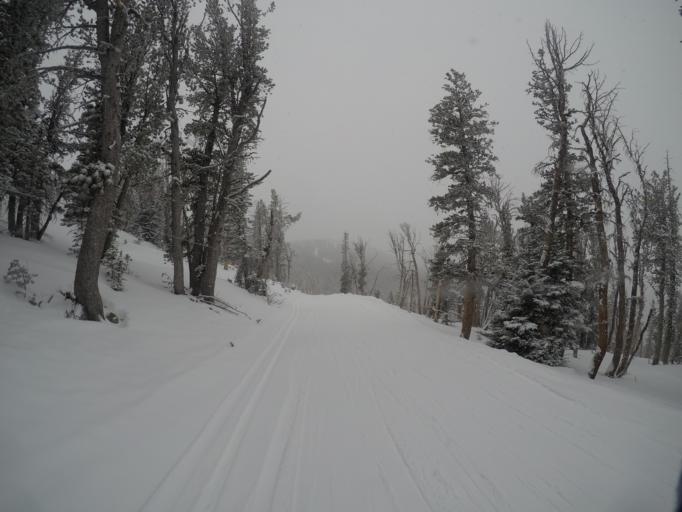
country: US
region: Montana
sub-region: Carbon County
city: Red Lodge
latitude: 45.1839
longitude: -109.3602
